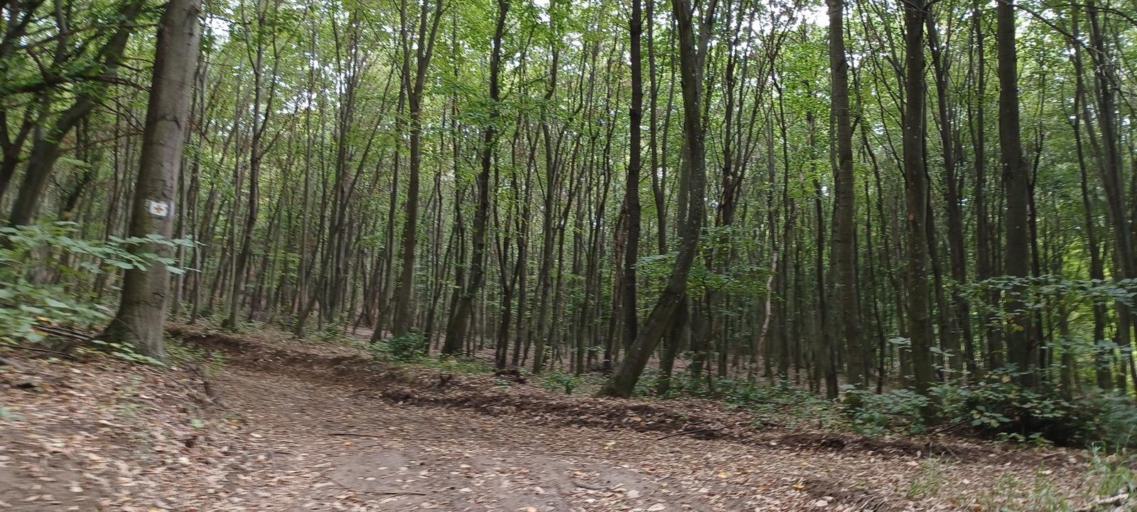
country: HU
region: Tolna
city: Szentgalpuszta
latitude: 46.3264
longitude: 18.6298
